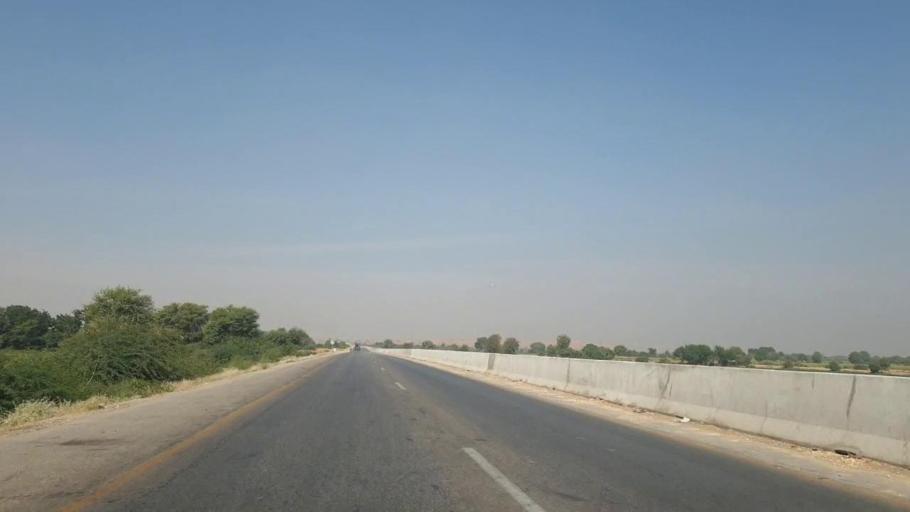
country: PK
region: Sindh
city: Matiari
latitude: 25.5941
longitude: 68.3087
